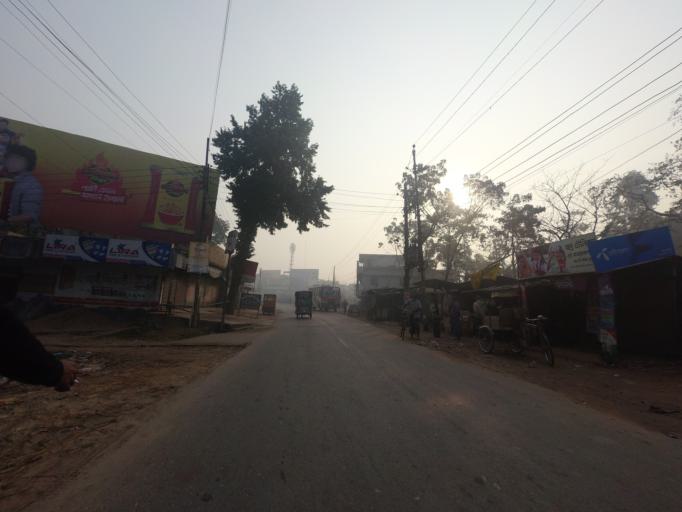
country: BD
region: Khulna
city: Narail
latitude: 23.1655
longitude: 89.4971
